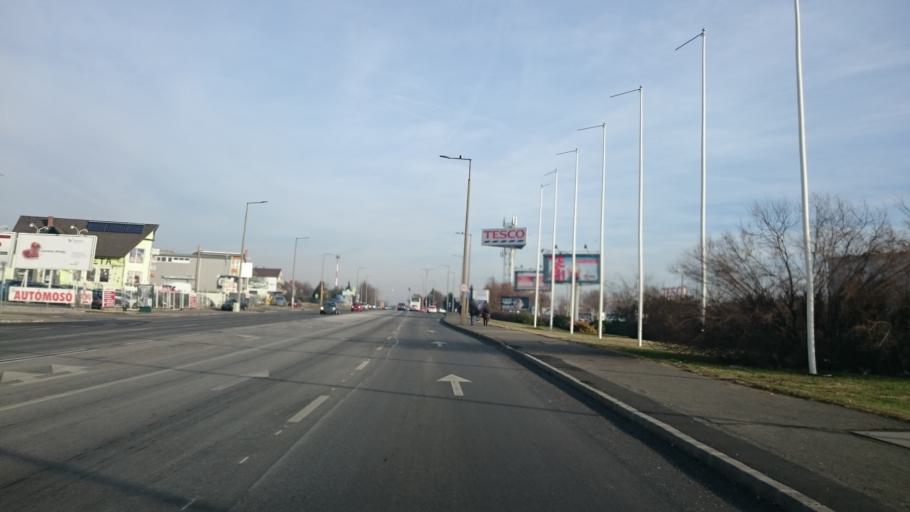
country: HU
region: Baranya
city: Pellerd
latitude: 46.0647
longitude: 18.1803
